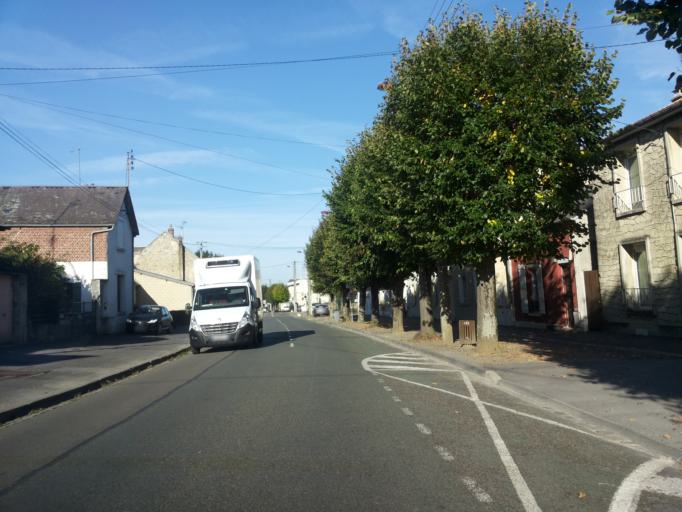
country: FR
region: Picardie
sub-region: Departement de l'Aisne
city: Laon
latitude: 49.5704
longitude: 3.5983
